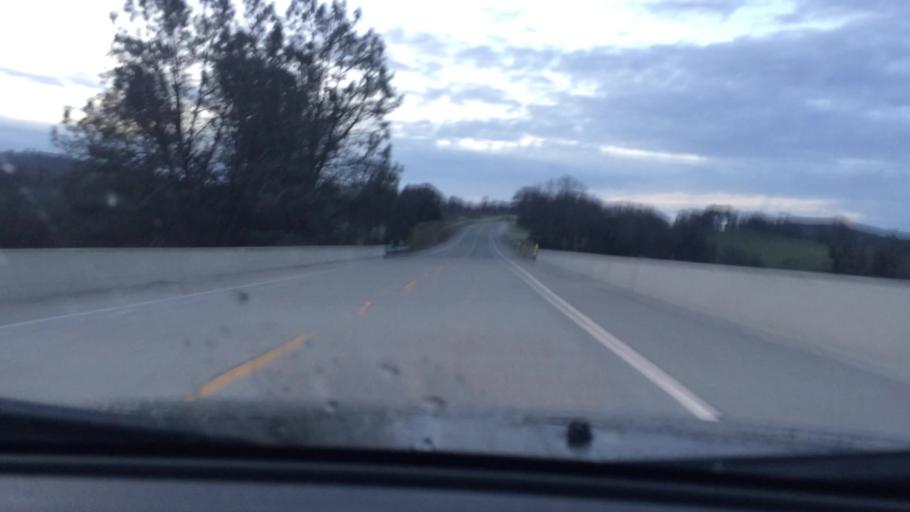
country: US
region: California
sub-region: Amador County
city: Plymouth
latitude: 38.4289
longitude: -120.8766
